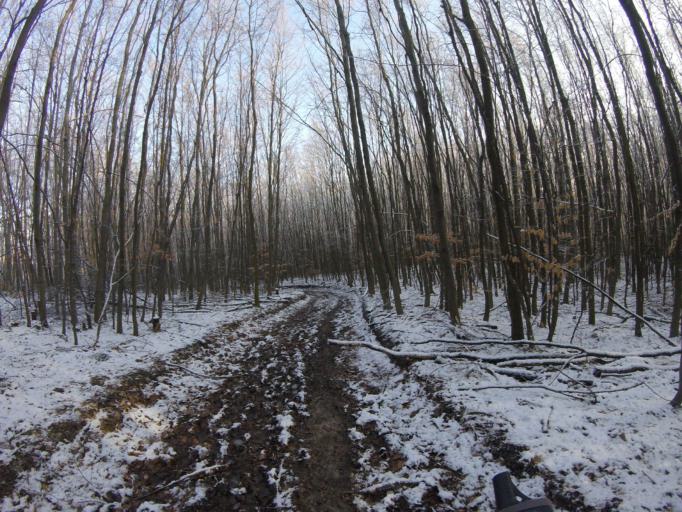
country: HU
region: Komarom-Esztergom
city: Pilismarot
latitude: 47.7287
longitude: 18.8588
